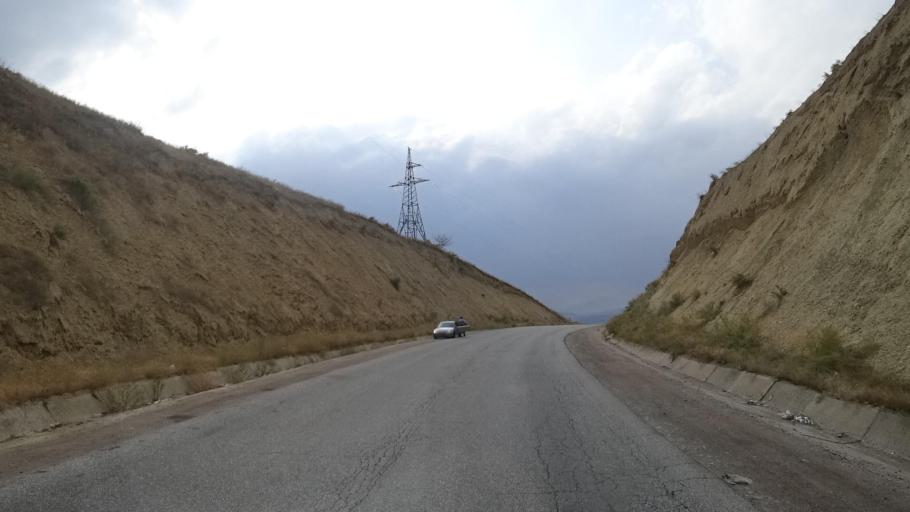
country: KG
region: Jalal-Abad
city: Uch-Terek
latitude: 41.8195
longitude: 73.1839
